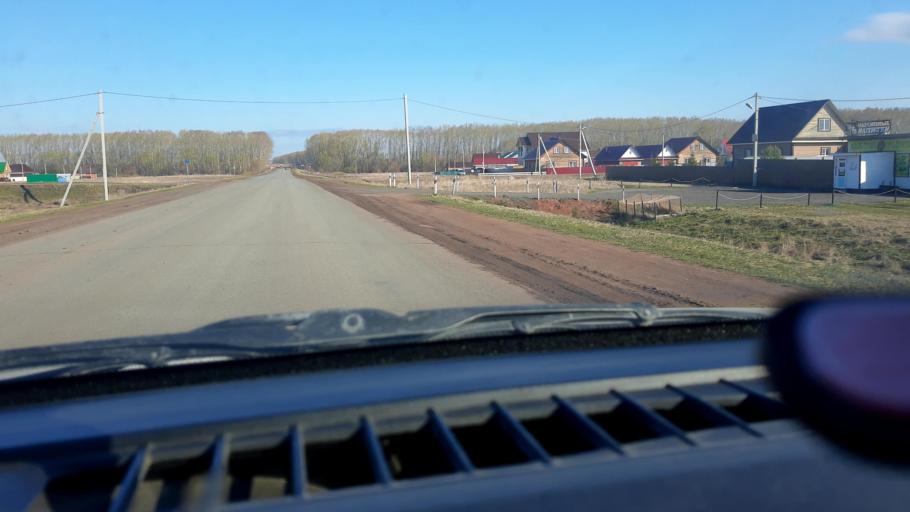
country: RU
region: Bashkortostan
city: Asanovo
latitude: 54.9669
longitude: 55.5430
